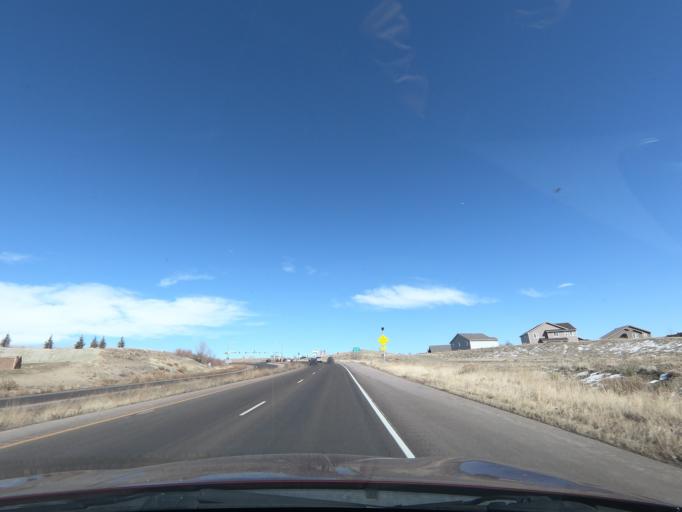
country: US
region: Colorado
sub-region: El Paso County
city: Fountain
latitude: 38.7196
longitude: -104.6838
